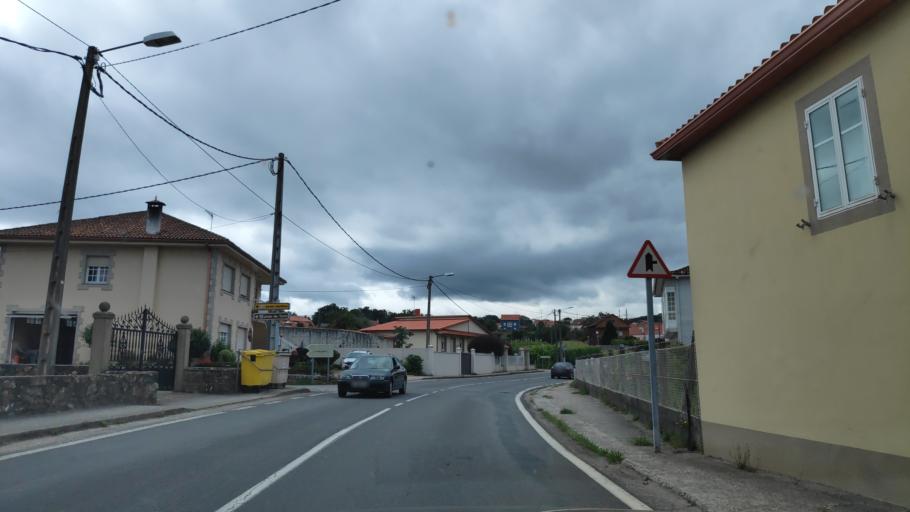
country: ES
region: Galicia
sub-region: Provincia da Coruna
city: Rianxo
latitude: 42.6700
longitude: -8.8150
